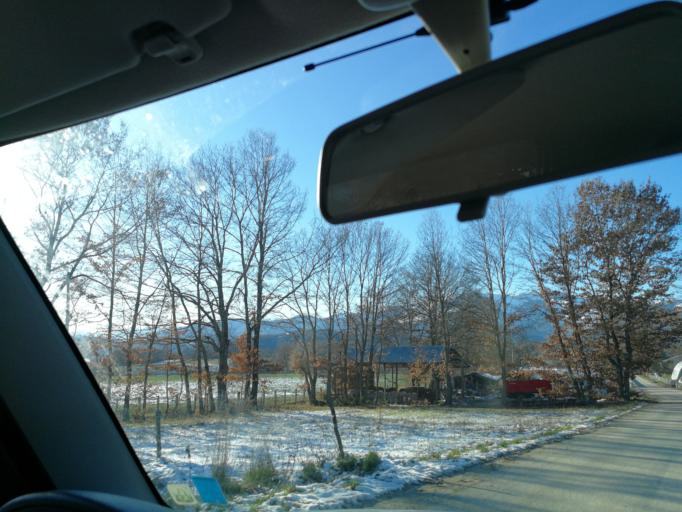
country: IT
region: Latium
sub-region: Provincia di Rieti
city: Amatrice
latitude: 42.6562
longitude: 13.2917
